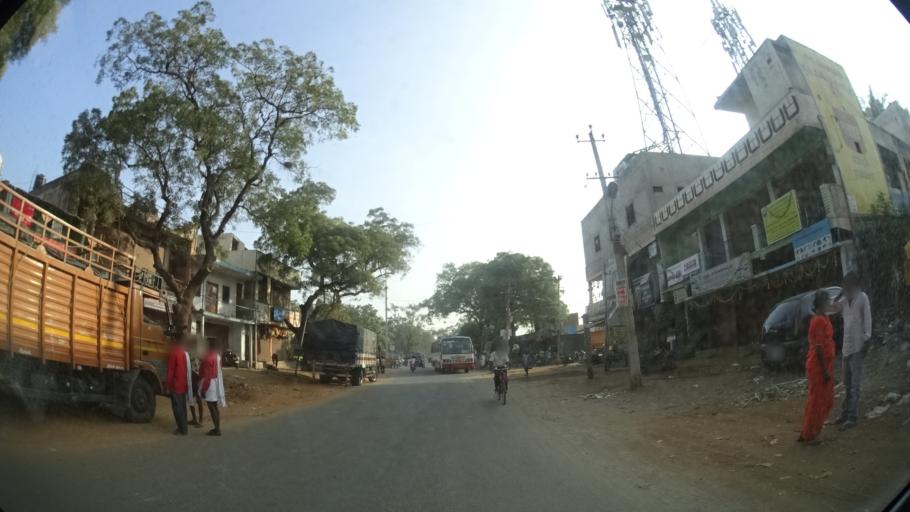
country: IN
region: Karnataka
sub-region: Bellary
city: Hospet
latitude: 15.2611
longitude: 76.3818
